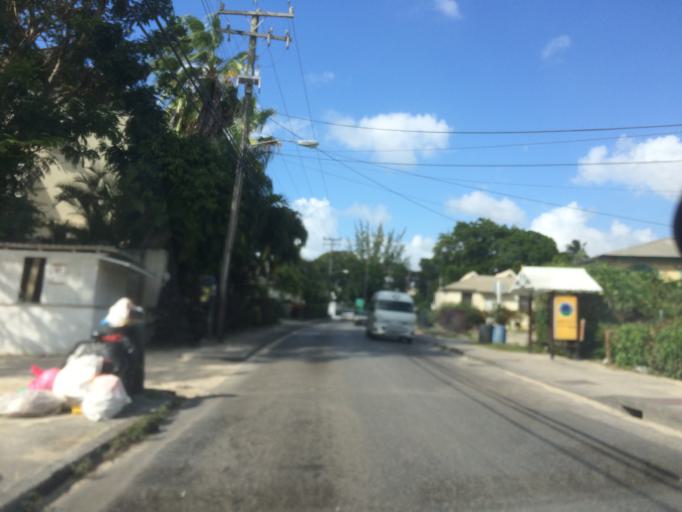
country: BB
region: Saint James
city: Holetown
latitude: 13.1602
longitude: -59.6373
